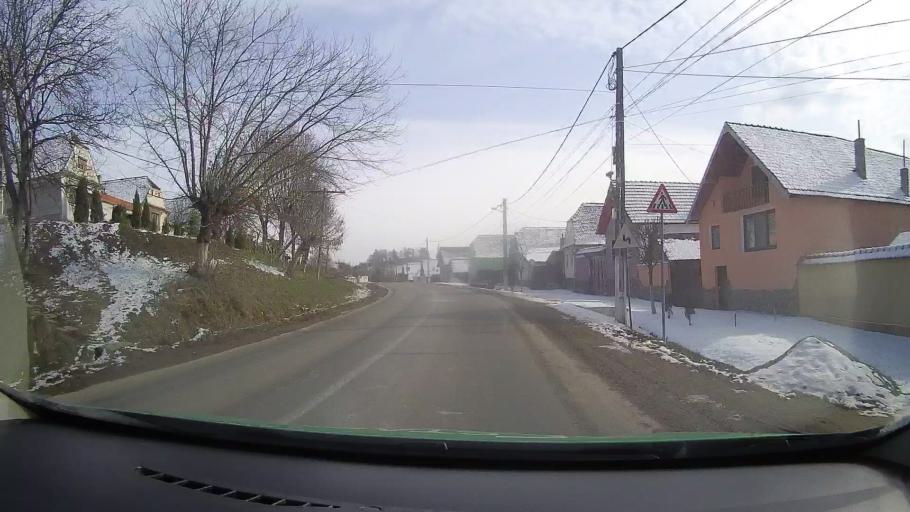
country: RO
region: Mures
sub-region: Comuna Apold
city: Saes
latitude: 46.1599
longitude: 24.7633
